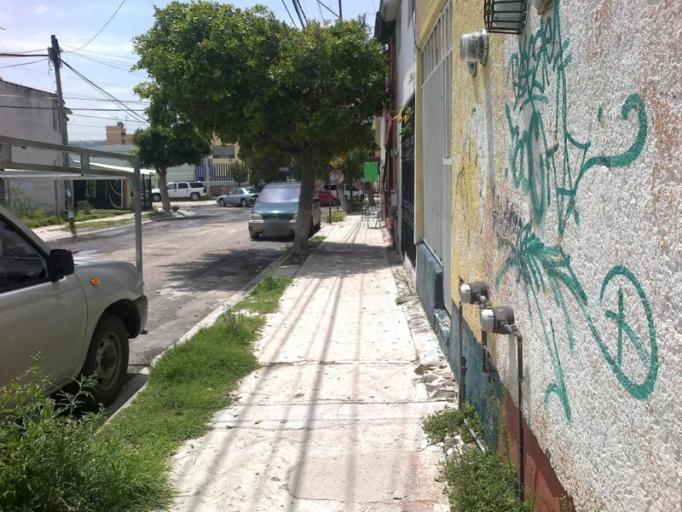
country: MX
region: Queretaro
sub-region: Queretaro
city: Sergio Villasenor
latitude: 20.6283
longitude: -100.4034
